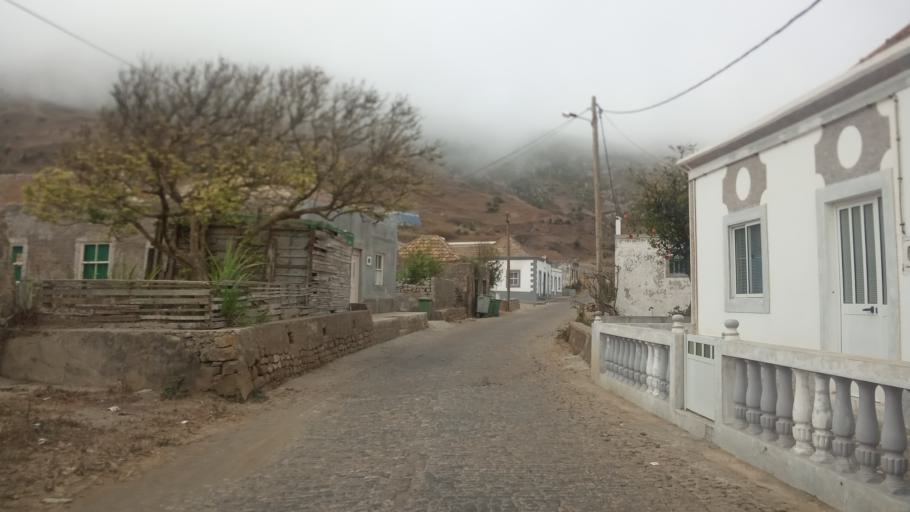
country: CV
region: Brava
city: Vila Nova Sintra
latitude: 14.8701
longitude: -24.7059
